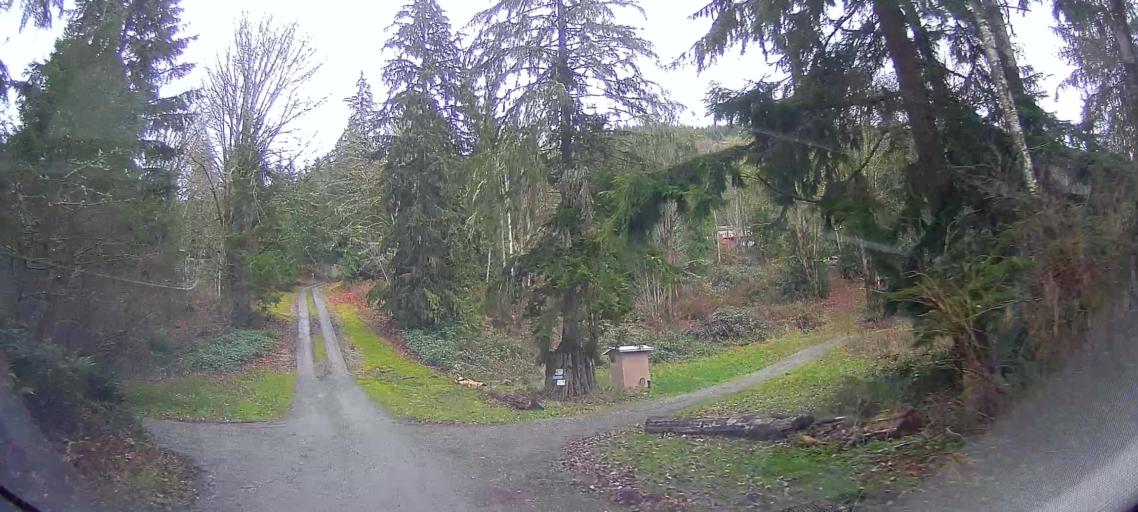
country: US
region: Washington
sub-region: Skagit County
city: Sedro-Woolley
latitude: 48.5955
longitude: -122.2134
